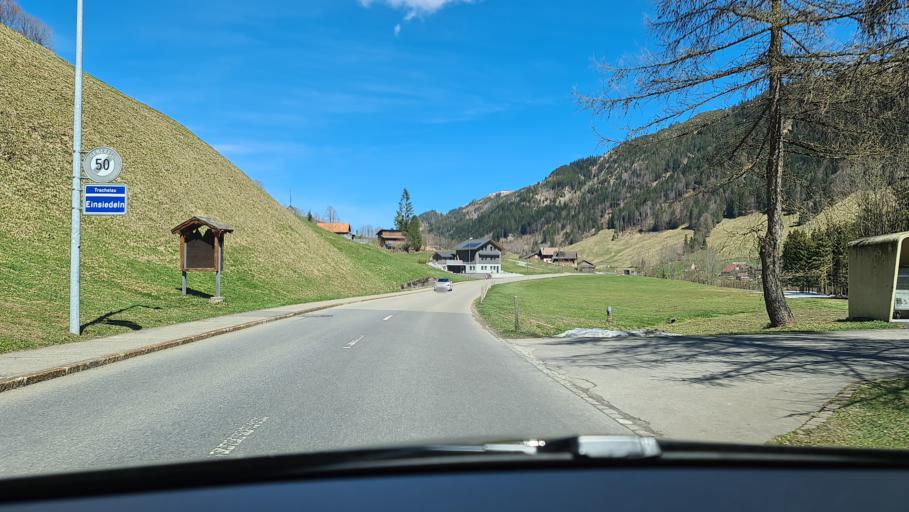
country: CH
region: Schwyz
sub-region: Bezirk Schwyz
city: Rothenthurm
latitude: 47.0723
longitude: 8.7172
